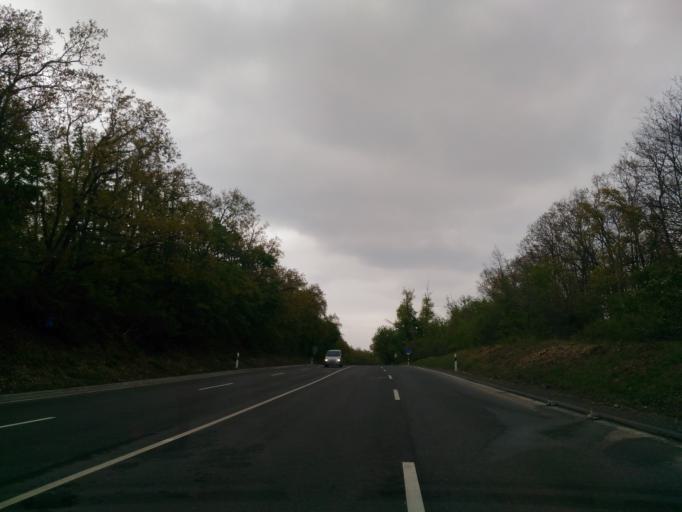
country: HU
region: Pest
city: Kerepes
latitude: 47.5813
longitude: 19.2926
